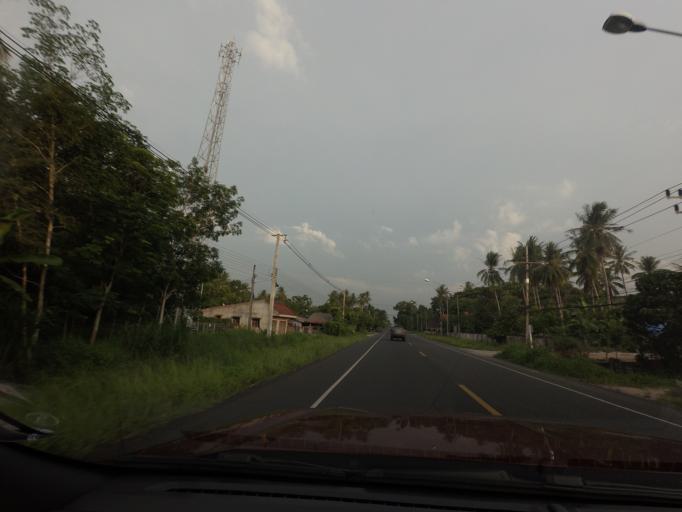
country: TH
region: Pattani
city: Mae Lan
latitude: 6.6113
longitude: 101.1912
